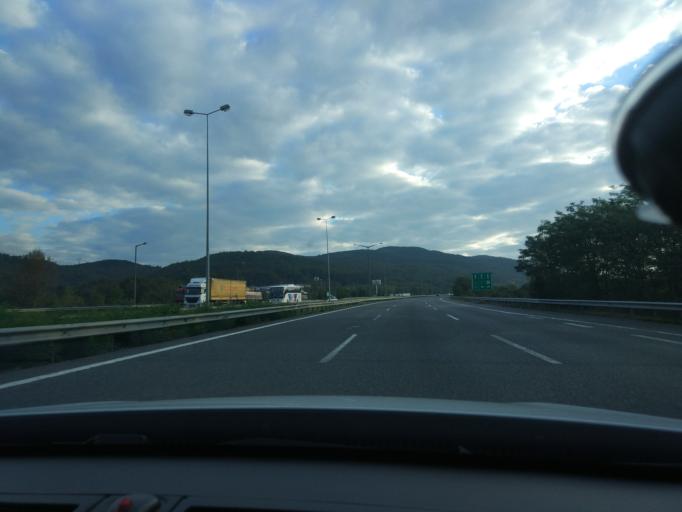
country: TR
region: Sakarya
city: Karadere
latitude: 40.8048
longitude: 30.8543
